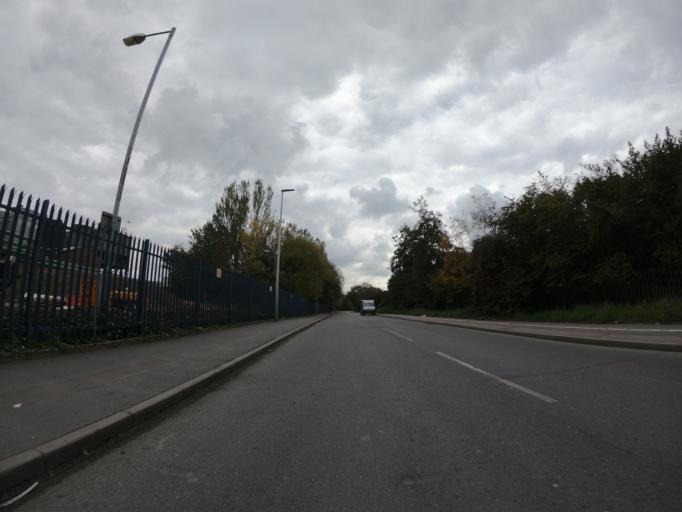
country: GB
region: England
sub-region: Greater London
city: Erith
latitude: 51.4922
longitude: 0.1679
